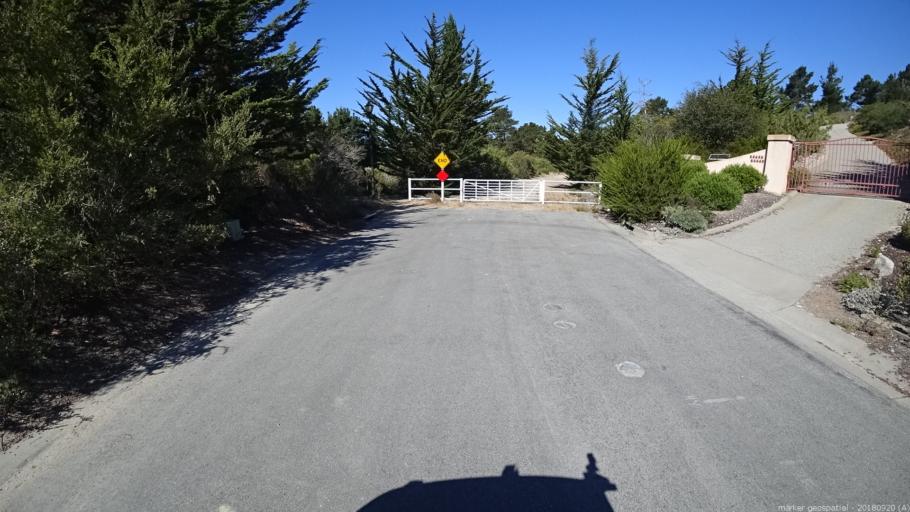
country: US
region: California
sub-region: Monterey County
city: Carmel-by-the-Sea
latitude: 36.5623
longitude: -121.9014
